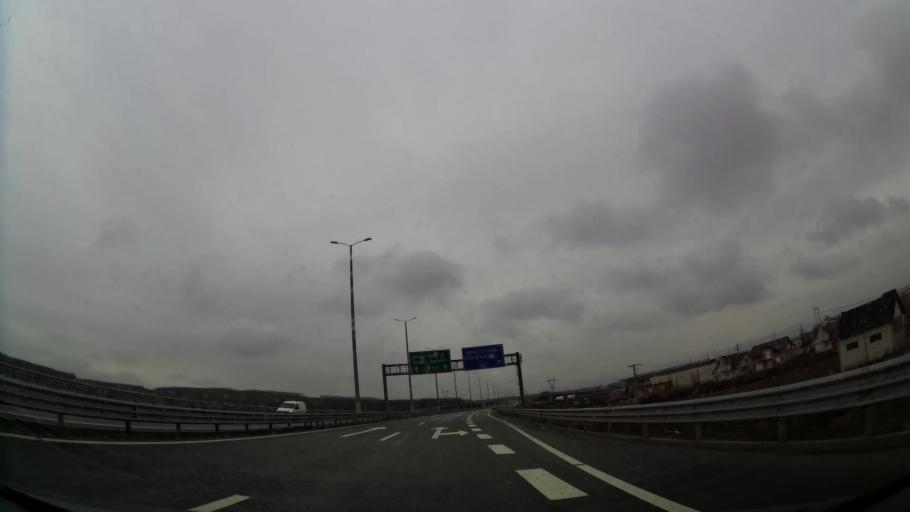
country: XK
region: Ferizaj
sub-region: Komuna e Ferizajt
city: Ferizaj
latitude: 42.3716
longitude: 21.2068
